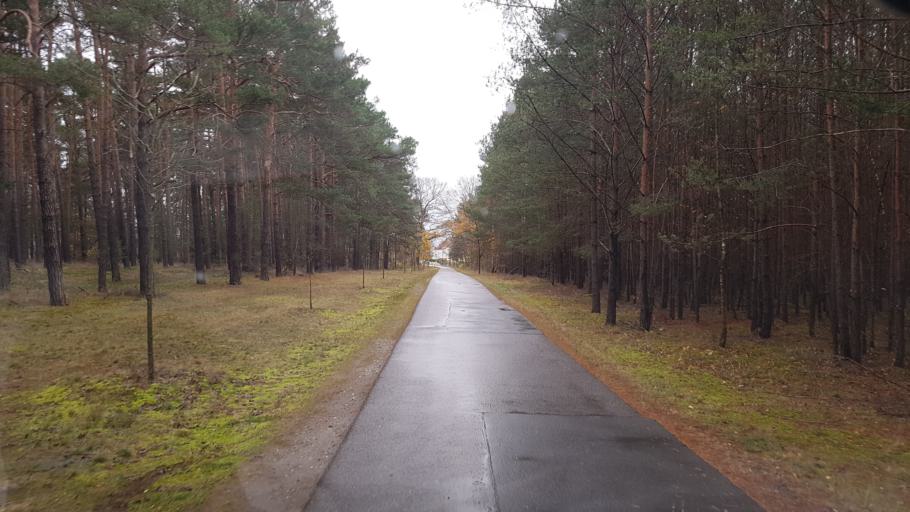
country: DE
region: Brandenburg
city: Tettau
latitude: 51.4245
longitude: 13.7677
